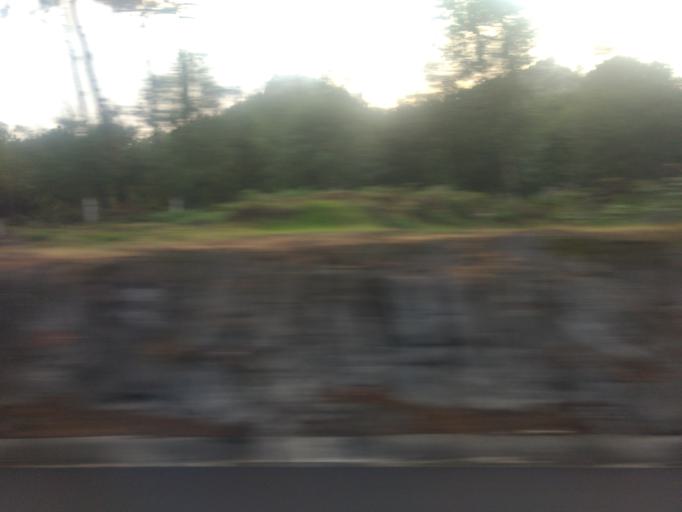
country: MX
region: Veracruz
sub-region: Acajete
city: La Joya
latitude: 19.6264
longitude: -97.0276
